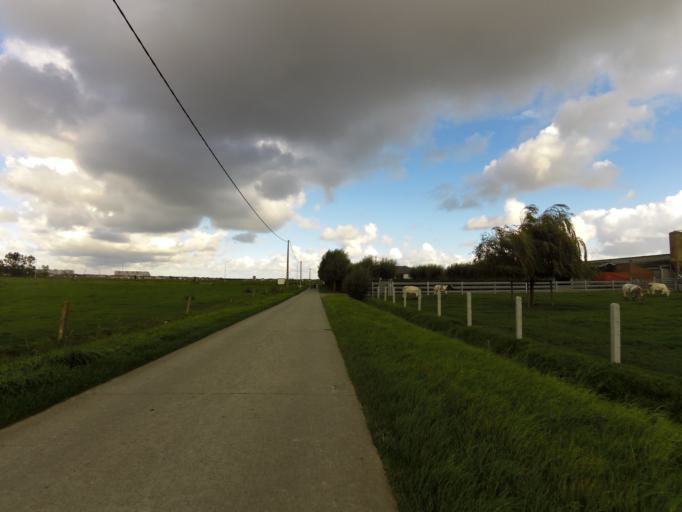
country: BE
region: Flanders
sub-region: Provincie West-Vlaanderen
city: Middelkerke
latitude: 51.1819
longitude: 2.8481
